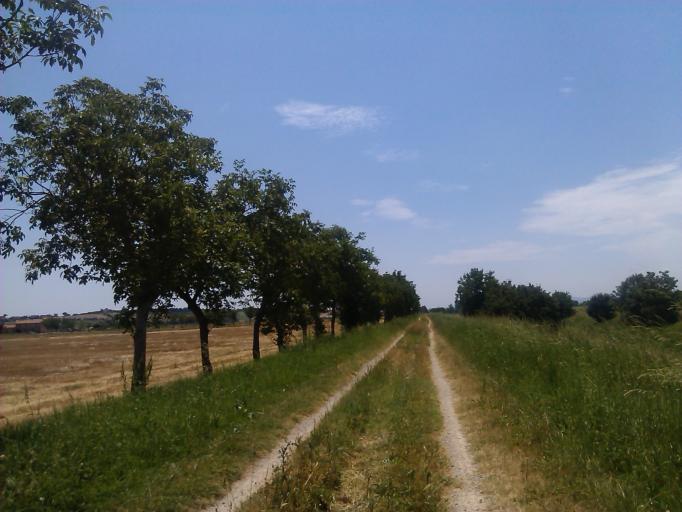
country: IT
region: Tuscany
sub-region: Province of Arezzo
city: Cesa
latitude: 43.3075
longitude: 11.8391
